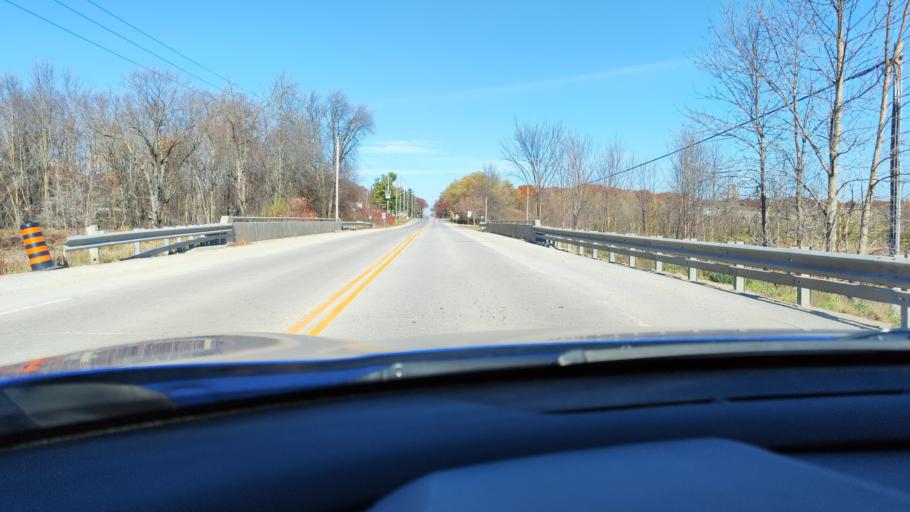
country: CA
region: Ontario
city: Wasaga Beach
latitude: 44.4611
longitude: -80.0729
